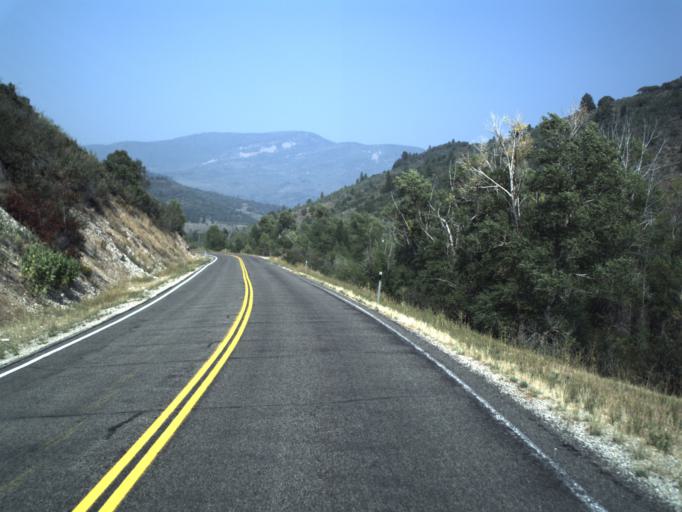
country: US
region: Utah
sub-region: Summit County
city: Francis
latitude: 40.6182
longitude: -111.2075
